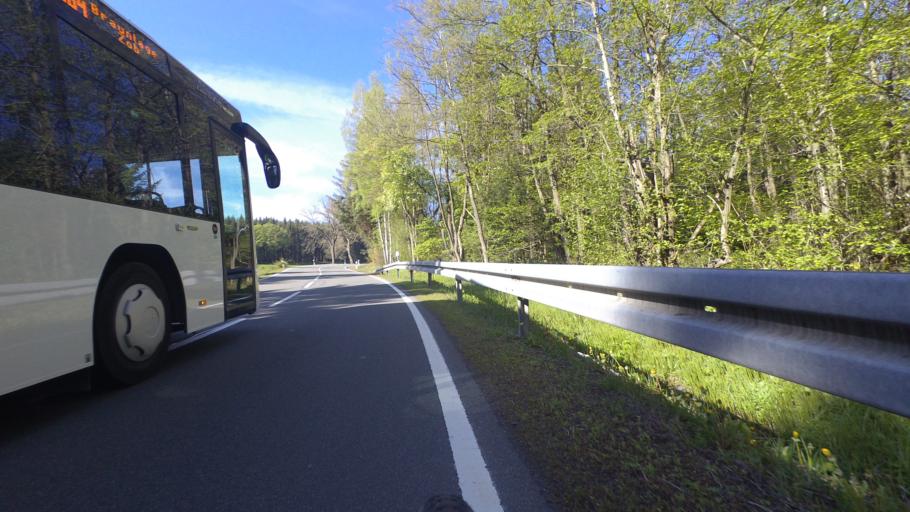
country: DE
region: Lower Saxony
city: Braunlage
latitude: 51.7571
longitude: 10.6949
